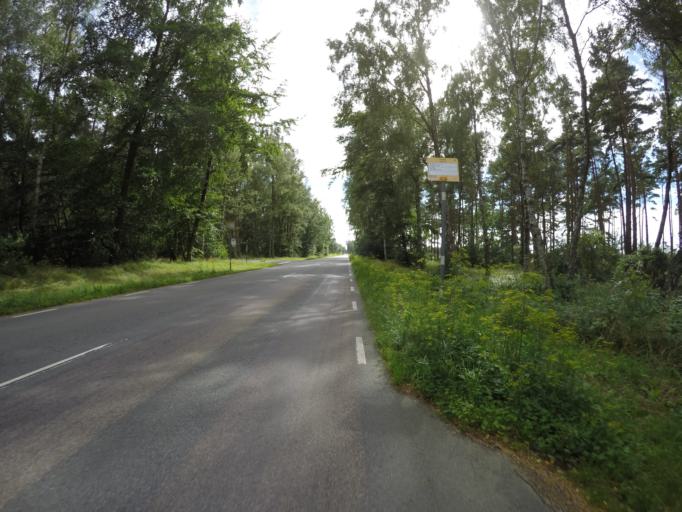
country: SE
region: Skane
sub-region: Simrishamns Kommun
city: Simrishamn
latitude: 55.4237
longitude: 14.2152
